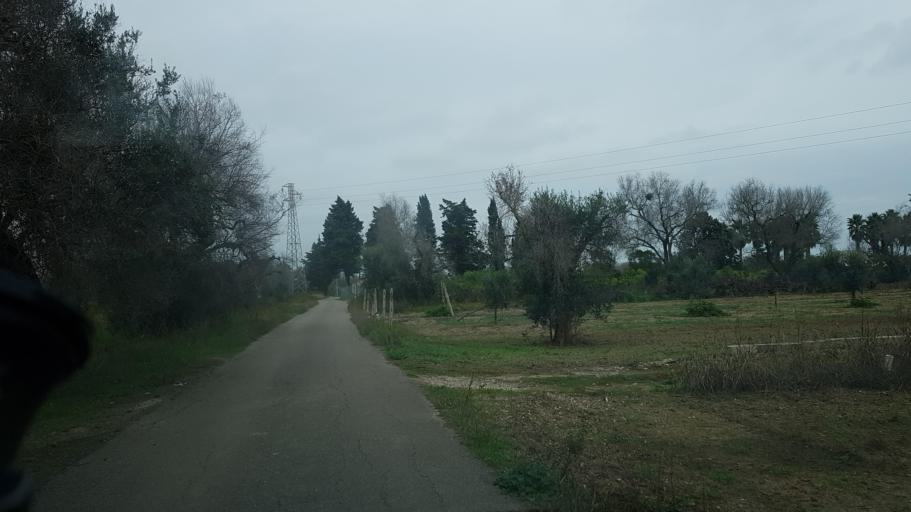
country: IT
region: Apulia
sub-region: Provincia di Brindisi
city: San Donaci
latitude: 40.4521
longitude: 17.9358
